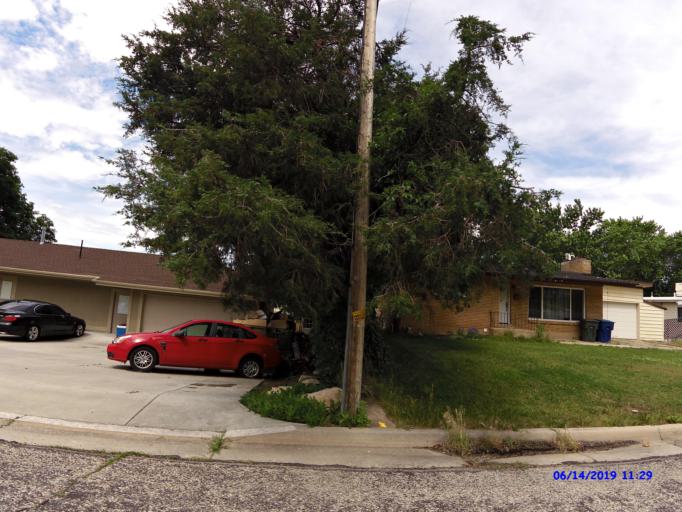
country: US
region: Utah
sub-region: Weber County
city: Ogden
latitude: 41.2589
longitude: -111.9426
